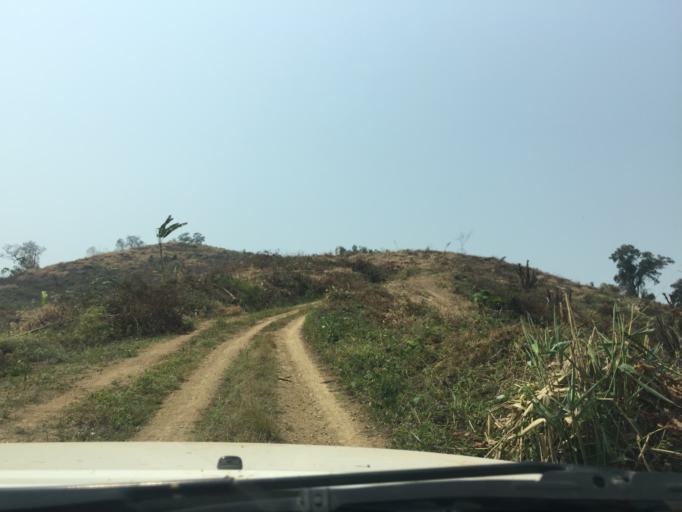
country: LA
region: Loungnamtha
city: Muang Nale
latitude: 20.6204
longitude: 101.6143
